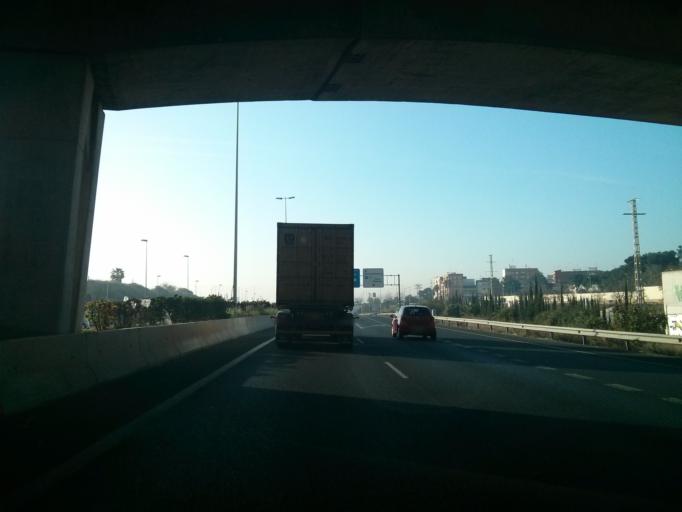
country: ES
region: Valencia
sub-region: Provincia de Valencia
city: Paterna
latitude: 39.5016
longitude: -0.4305
